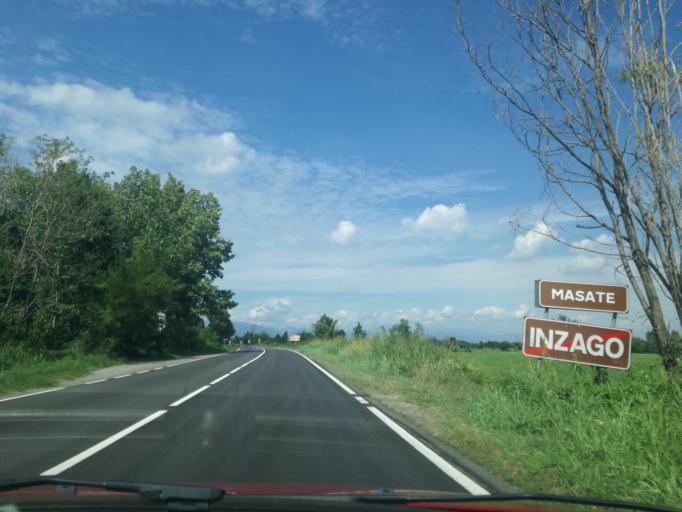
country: IT
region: Lombardy
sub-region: Citta metropolitana di Milano
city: Masate
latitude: 45.5531
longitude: 9.4574
